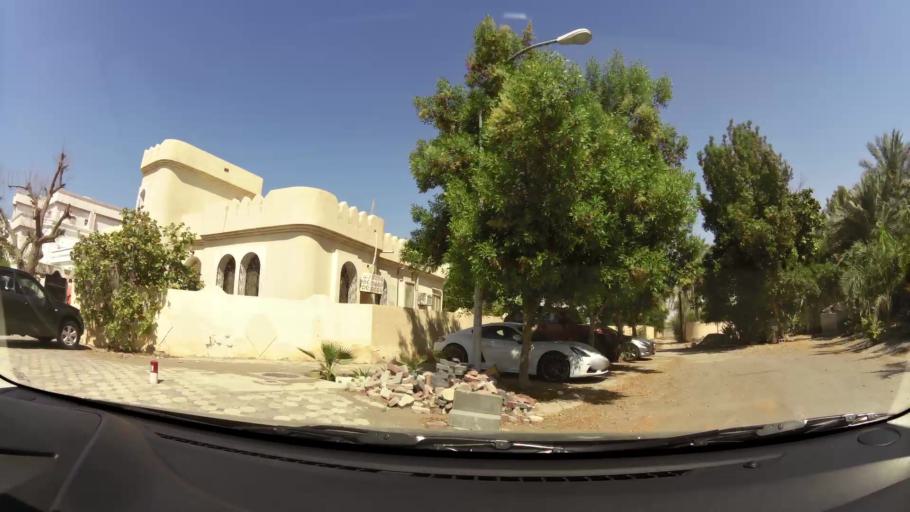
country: OM
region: Muhafazat Masqat
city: As Sib al Jadidah
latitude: 23.6376
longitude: 58.2232
